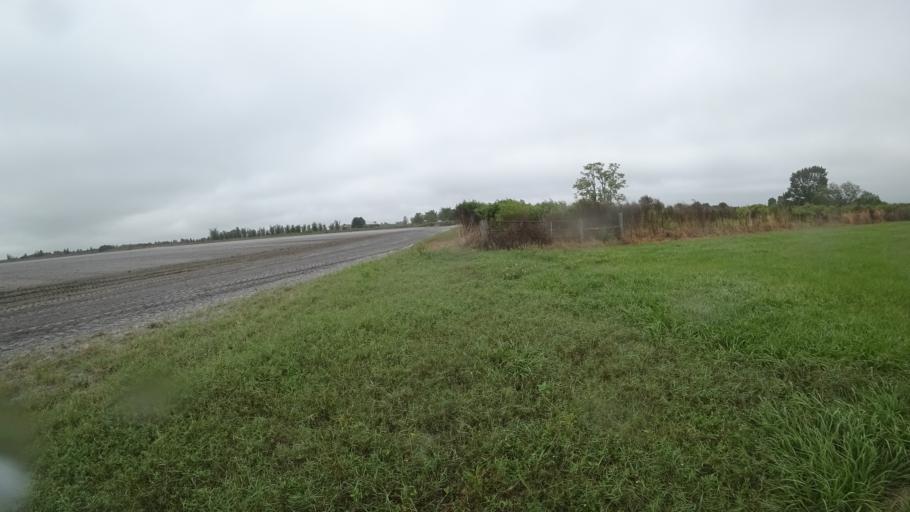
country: US
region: Florida
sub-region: Sarasota County
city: Warm Mineral Springs
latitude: 27.2961
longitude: -82.1769
